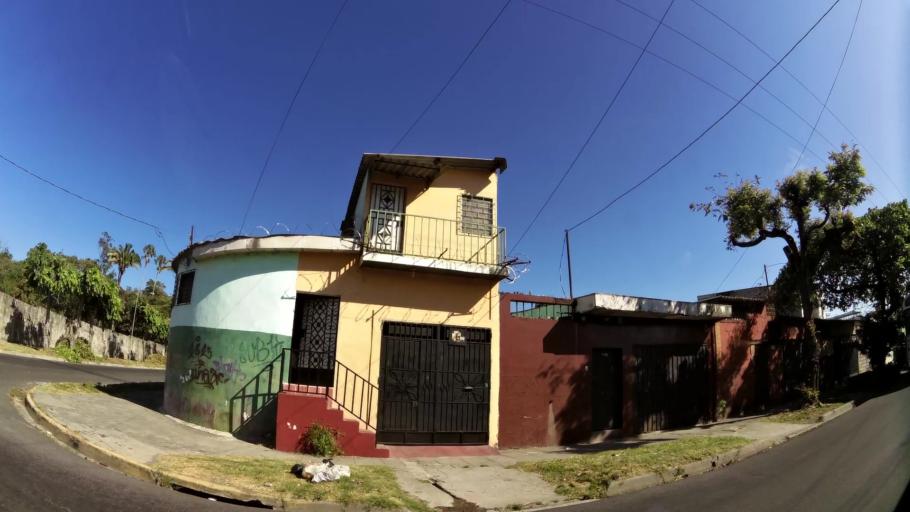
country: SV
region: La Libertad
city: Santa Tecla
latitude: 13.6778
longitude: -89.2955
